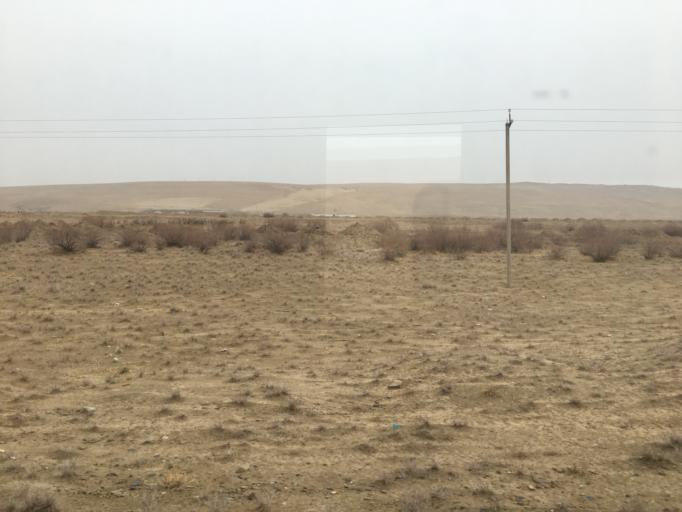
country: TM
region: Mary
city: Serhetabat
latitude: 35.5562
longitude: 62.5182
